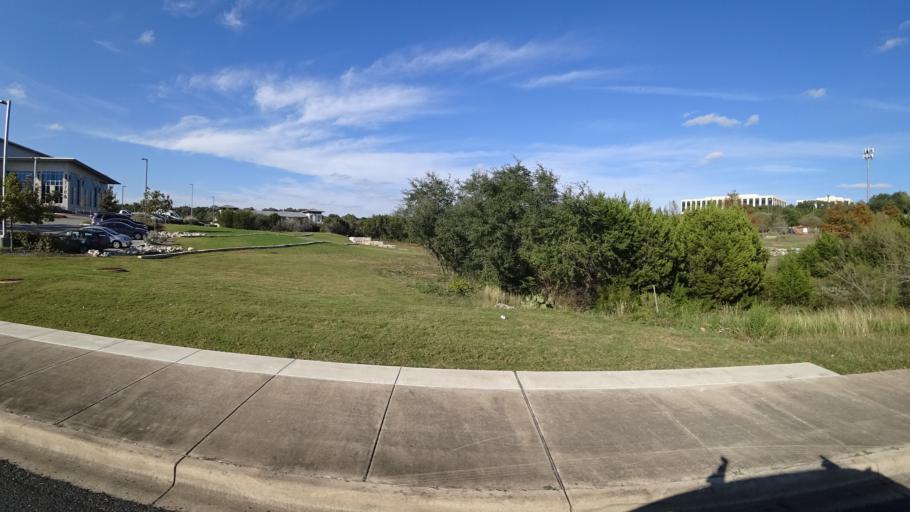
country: US
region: Texas
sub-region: Travis County
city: Barton Creek
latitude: 30.2536
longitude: -97.8743
